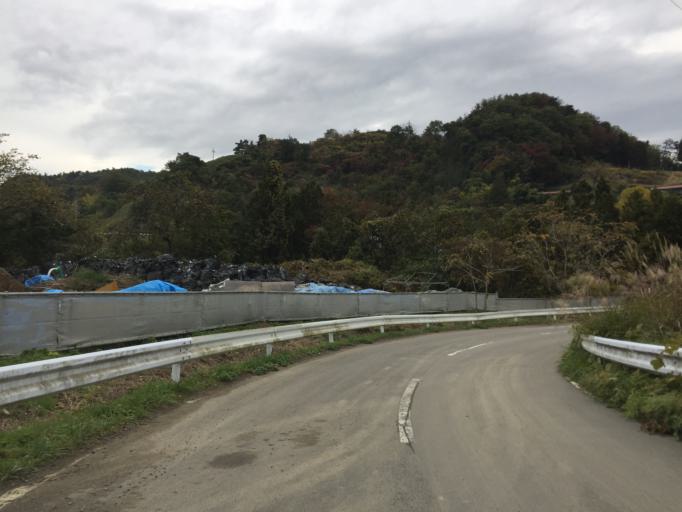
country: JP
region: Fukushima
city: Fukushima-shi
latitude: 37.8351
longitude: 140.4378
